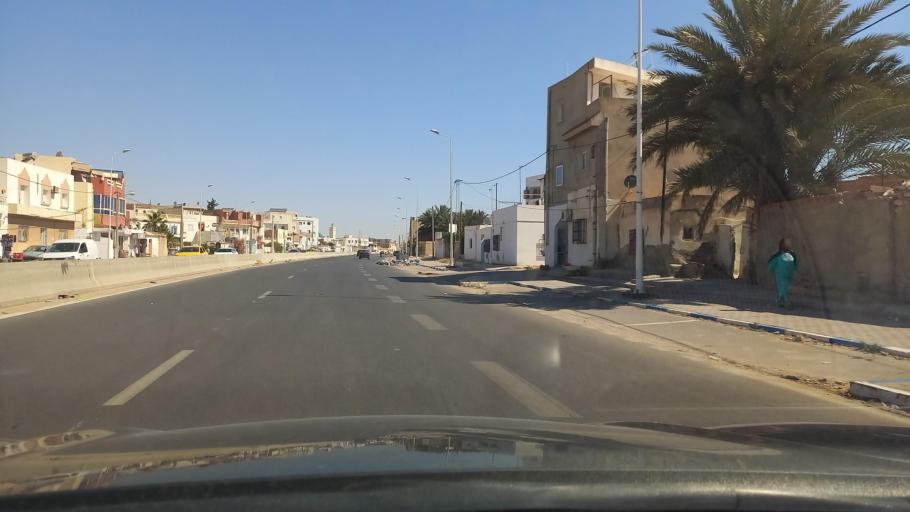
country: TN
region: Safaqis
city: Sfax
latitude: 34.7366
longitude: 10.7240
